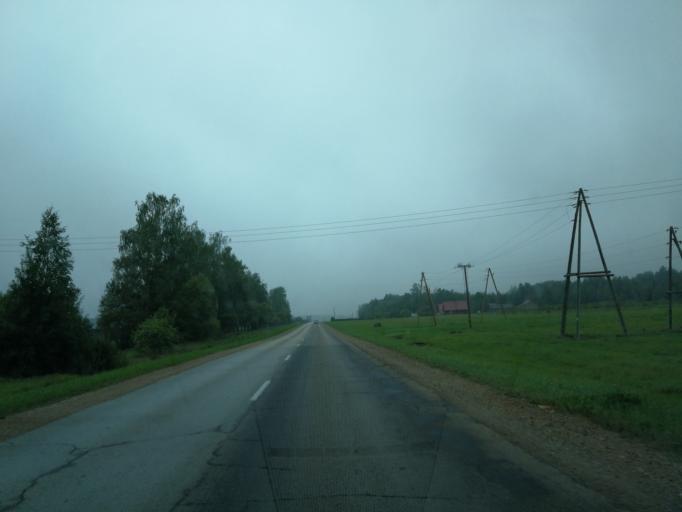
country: LV
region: Preilu Rajons
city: Preili
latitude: 56.2986
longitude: 26.6831
